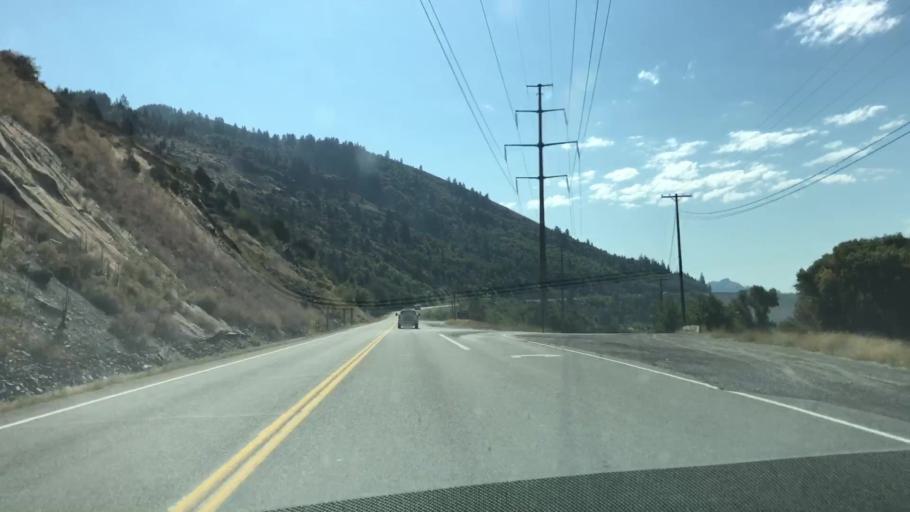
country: US
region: Idaho
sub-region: Teton County
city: Victor
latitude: 43.3456
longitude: -111.2079
